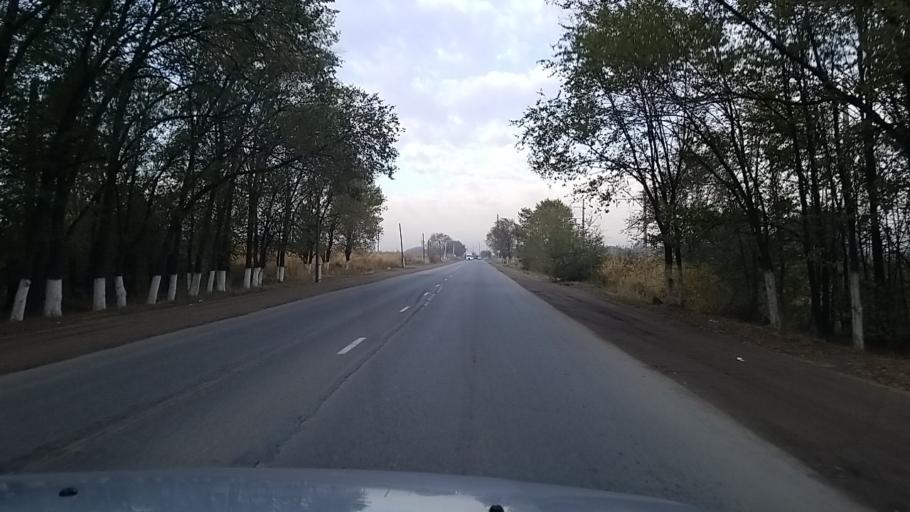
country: KZ
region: Almaty Oblysy
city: Burunday
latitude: 43.3567
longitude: 76.7916
